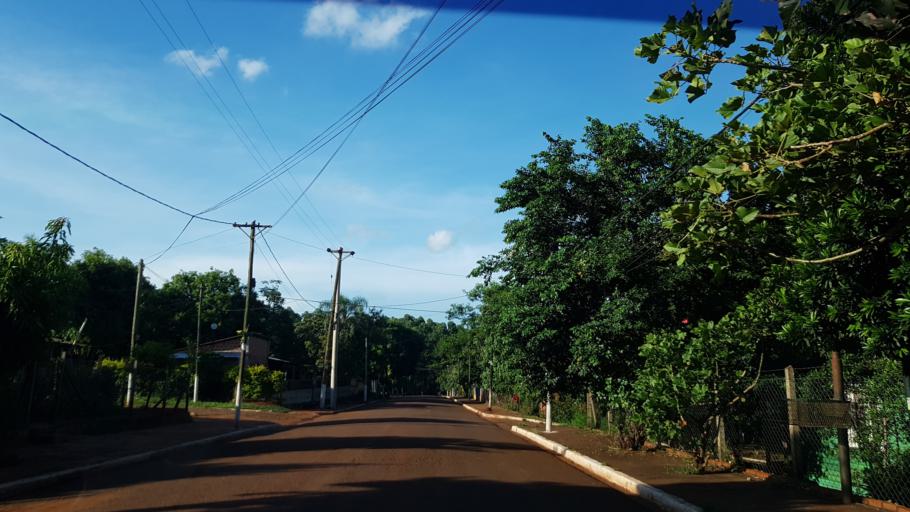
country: AR
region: Misiones
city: Puerto Libertad
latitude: -25.9174
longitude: -54.5878
